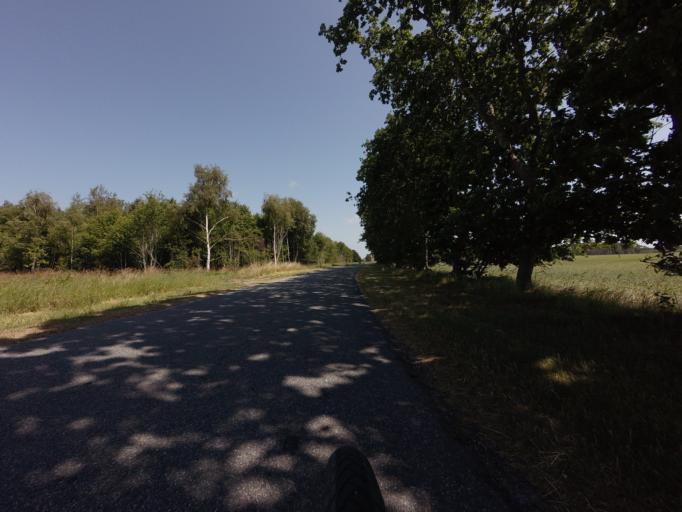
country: DK
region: North Denmark
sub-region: Laeso Kommune
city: Byrum
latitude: 57.2521
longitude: 10.9581
